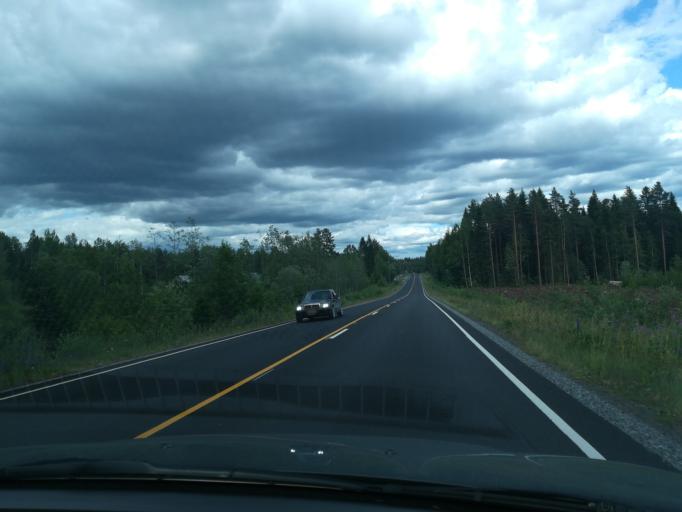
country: FI
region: Southern Savonia
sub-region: Mikkeli
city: Mikkeli
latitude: 61.6551
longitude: 27.0978
